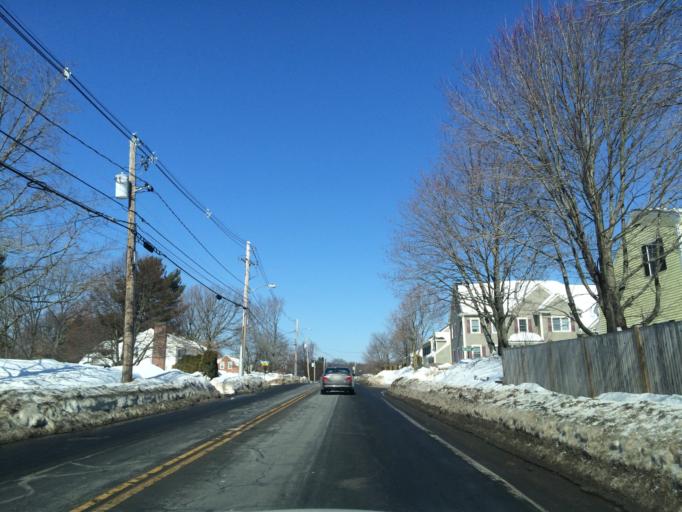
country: US
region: Massachusetts
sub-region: Norfolk County
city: Needham
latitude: 42.2973
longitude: -71.2464
